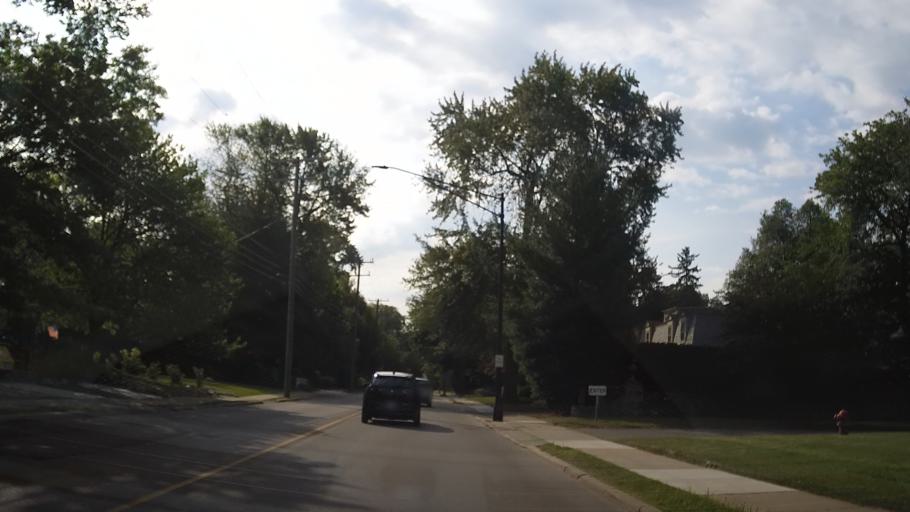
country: US
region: Michigan
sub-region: Wayne County
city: Grosse Pointe Farms
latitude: 42.4105
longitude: -82.8947
